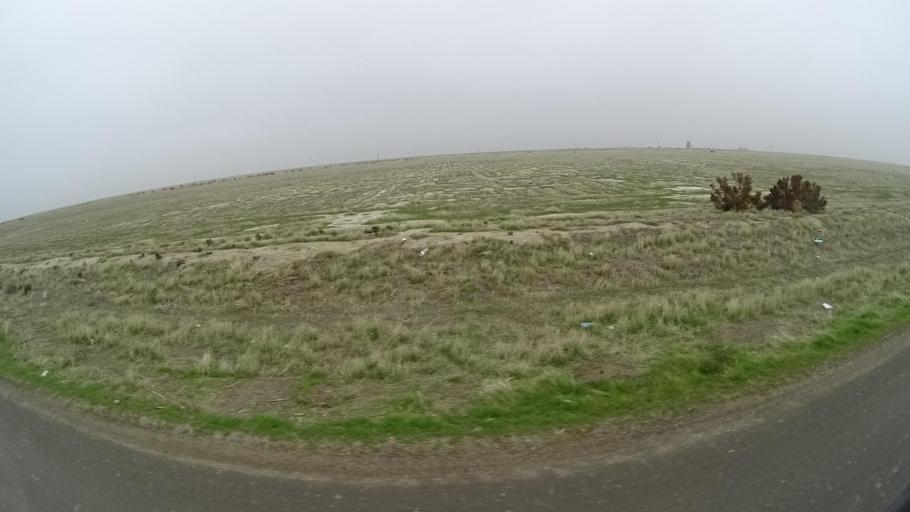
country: US
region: California
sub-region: Tulare County
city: Alpaugh
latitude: 35.7241
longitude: -119.4726
